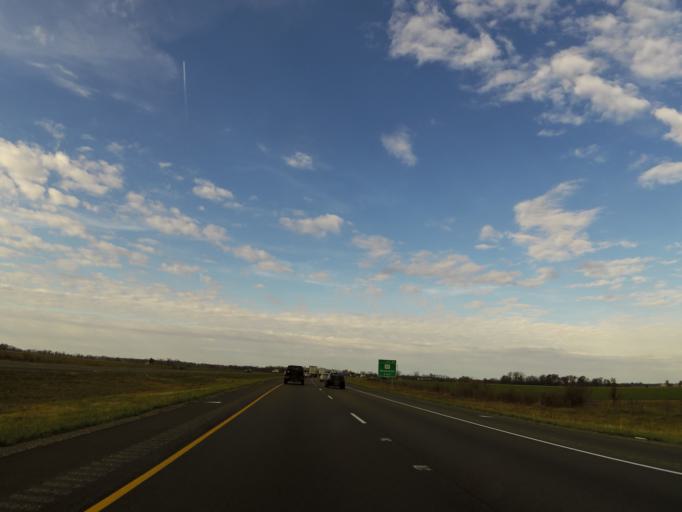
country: US
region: Illinois
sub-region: Washington County
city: Okawville
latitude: 38.4316
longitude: -89.5084
